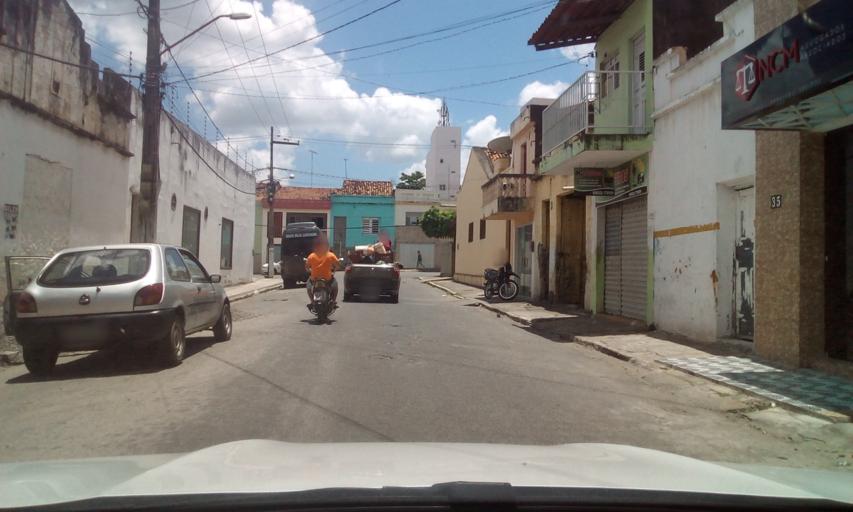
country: BR
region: Paraiba
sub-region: Guarabira
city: Guarabira
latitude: -6.8531
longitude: -35.4879
